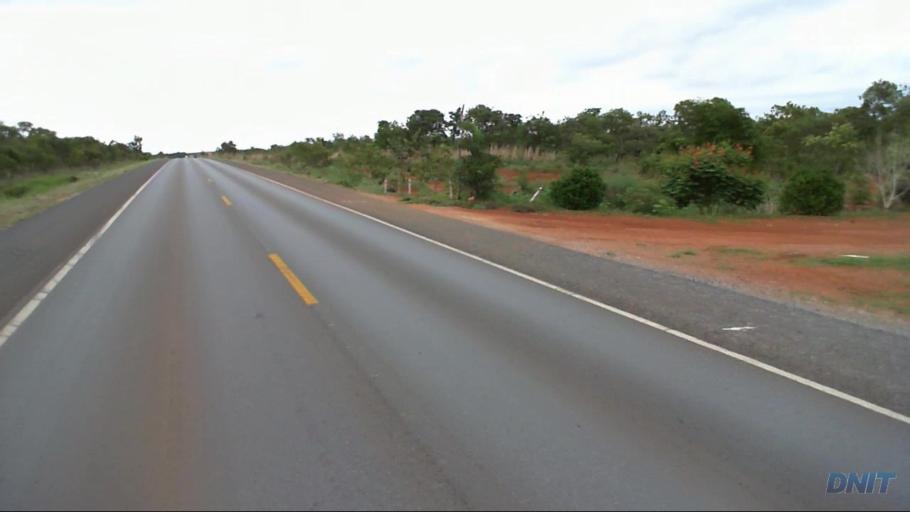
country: BR
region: Goias
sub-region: Barro Alto
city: Barro Alto
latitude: -15.2092
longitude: -48.6850
